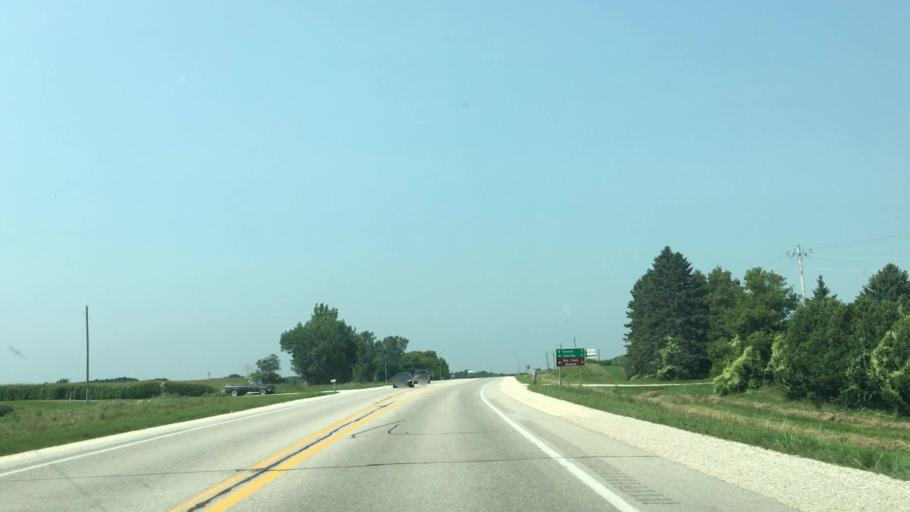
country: US
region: Iowa
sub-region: Winneshiek County
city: Decorah
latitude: 43.2028
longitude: -91.8771
